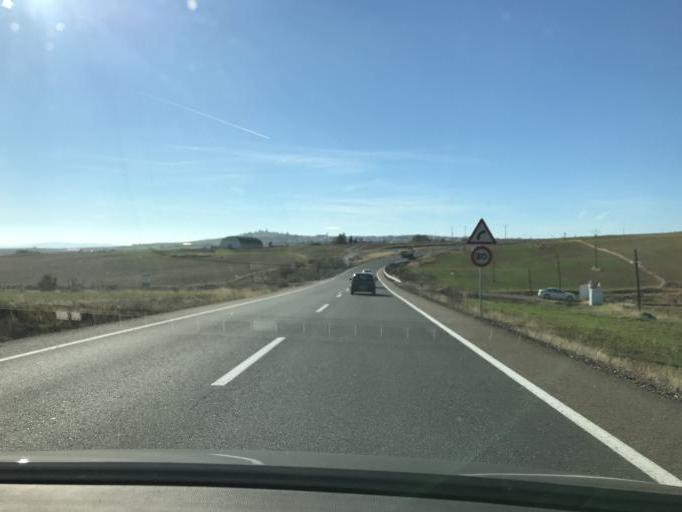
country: ES
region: Extremadura
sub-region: Provincia de Badajoz
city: Azuaga
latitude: 38.2809
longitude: -5.6613
